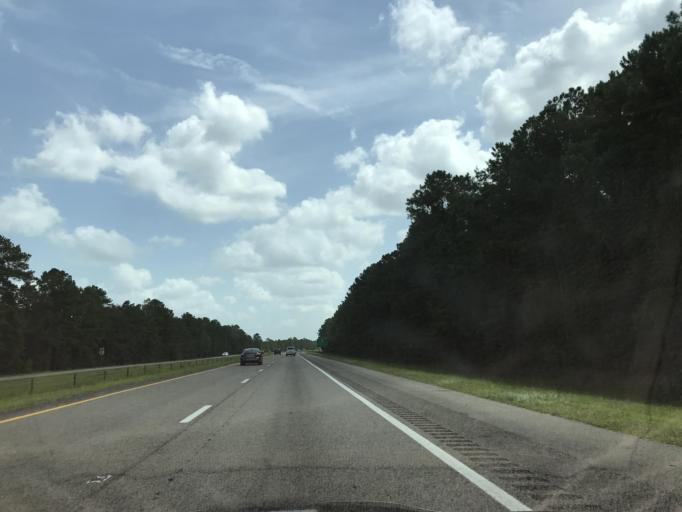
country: US
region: North Carolina
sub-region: Pender County
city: Burgaw
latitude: 34.5924
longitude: -77.9086
